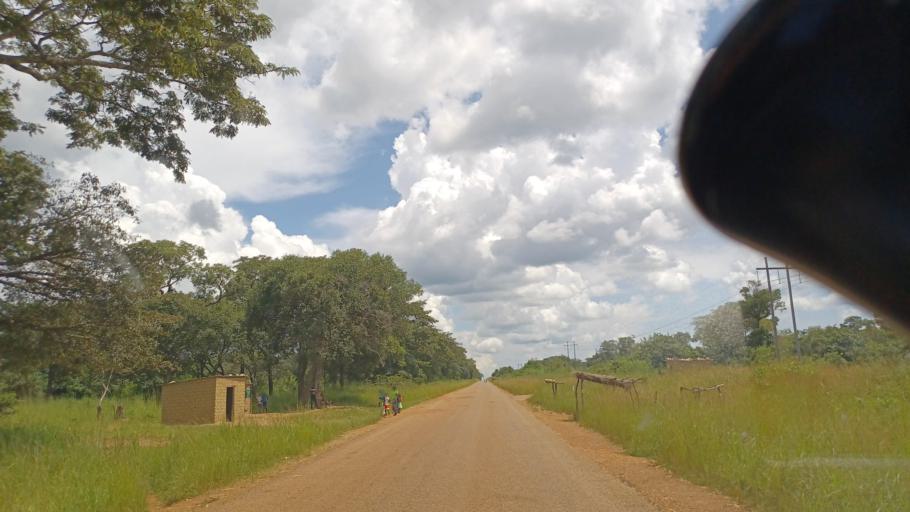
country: ZM
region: North-Western
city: Solwezi
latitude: -12.7004
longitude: 26.0361
